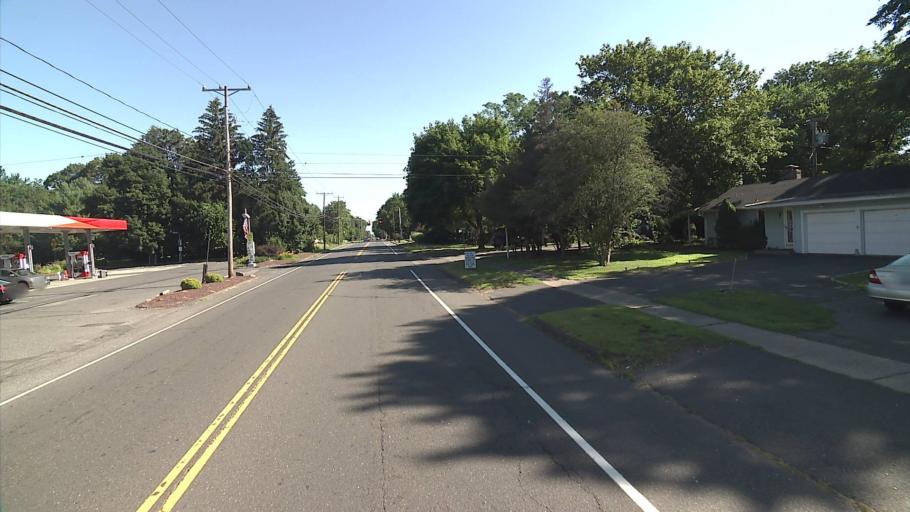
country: US
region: Connecticut
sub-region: New Haven County
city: Cheshire Village
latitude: 41.5141
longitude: -72.8986
